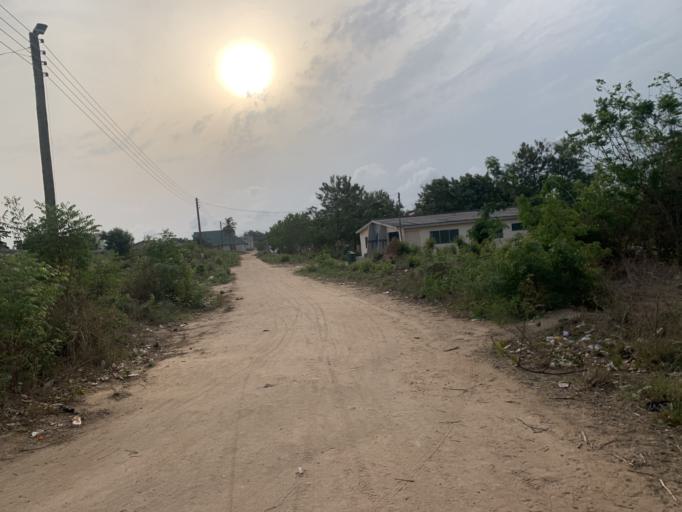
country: GH
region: Central
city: Winneba
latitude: 5.3607
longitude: -0.6247
